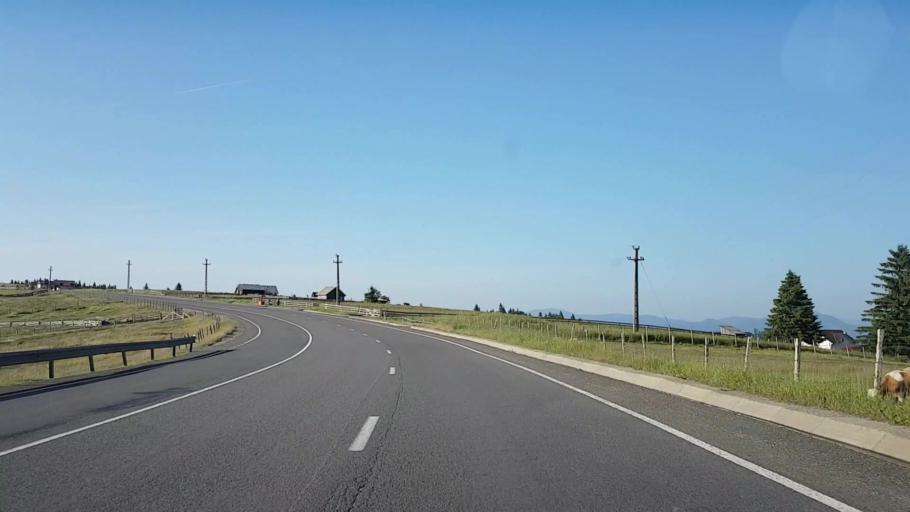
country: RO
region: Bistrita-Nasaud
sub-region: Comuna Lunca Ilvei
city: Lunca Ilvei
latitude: 47.2500
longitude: 25.0242
